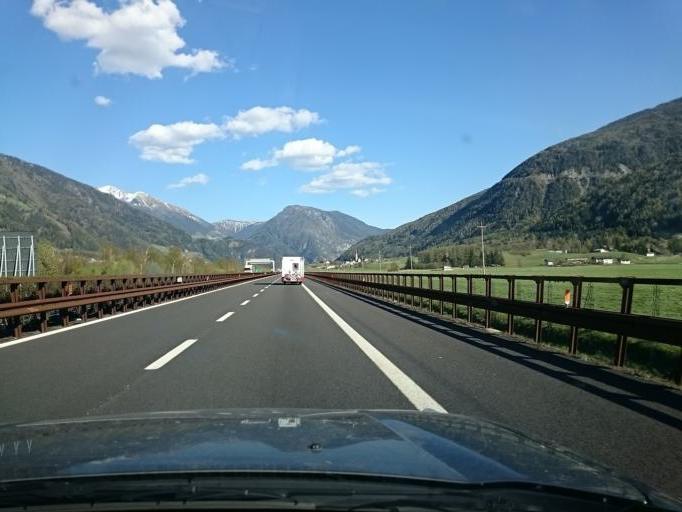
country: IT
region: Trentino-Alto Adige
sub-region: Bolzano
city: Prati
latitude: 46.8779
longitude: 11.4557
